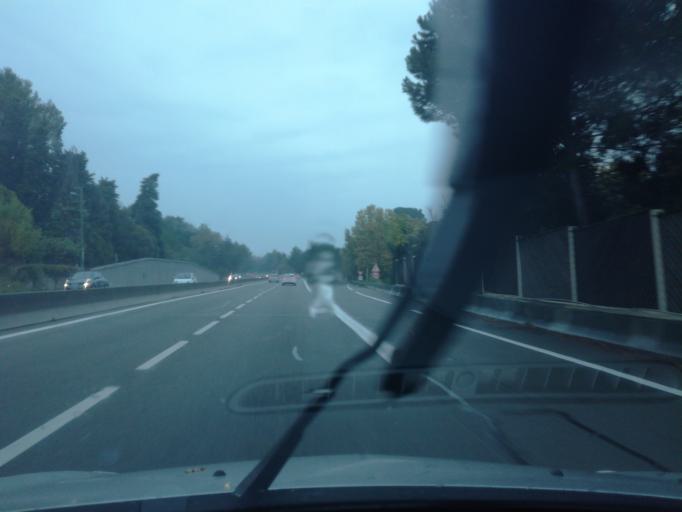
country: FR
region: Provence-Alpes-Cote d'Azur
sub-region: Departement des Alpes-Maritimes
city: Mougins
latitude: 43.5969
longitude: 7.0007
